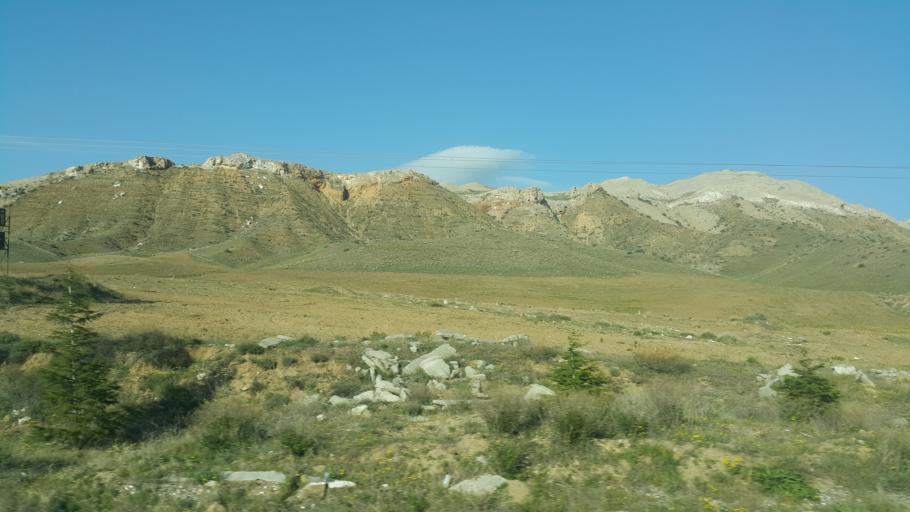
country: TR
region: Ankara
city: Sereflikochisar
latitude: 39.0004
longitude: 33.4649
